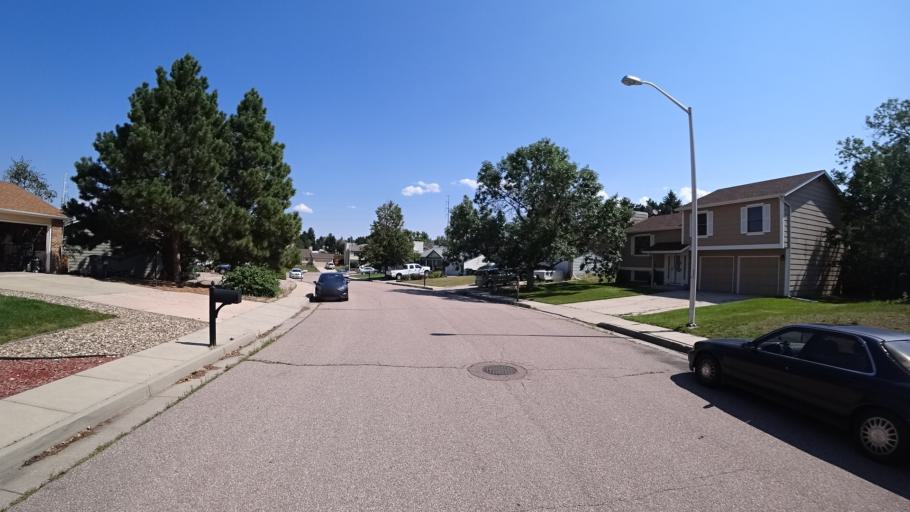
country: US
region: Colorado
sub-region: El Paso County
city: Air Force Academy
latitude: 38.9427
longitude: -104.7867
